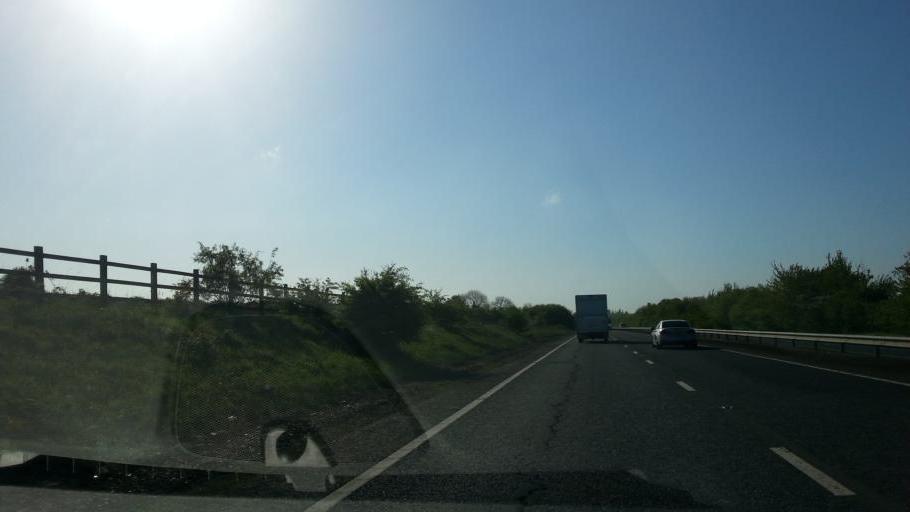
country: GB
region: England
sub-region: Peterborough
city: Castor
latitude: 52.5794
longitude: -0.3421
